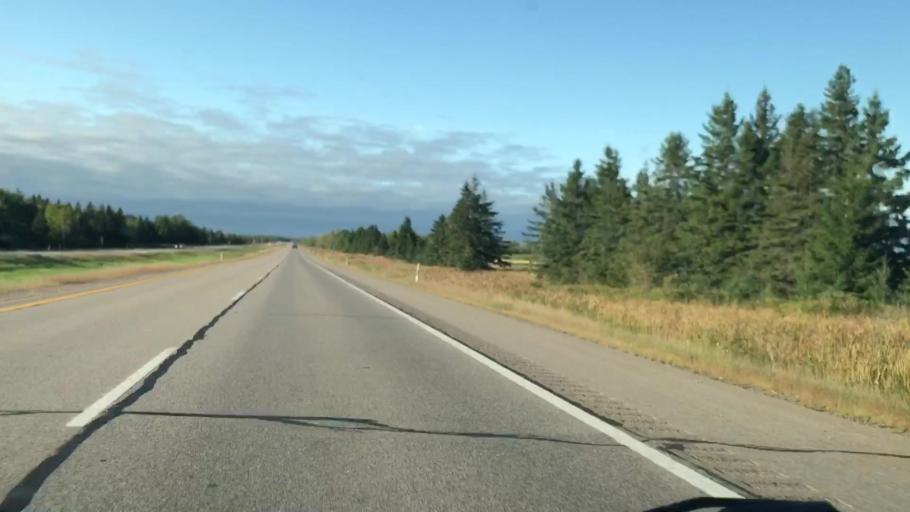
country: US
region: Michigan
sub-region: Chippewa County
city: Sault Ste. Marie
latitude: 46.4187
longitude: -84.3956
